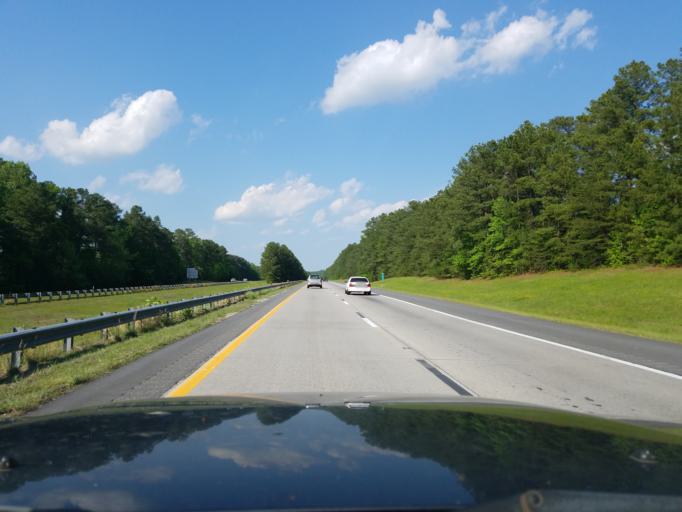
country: US
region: North Carolina
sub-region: Granville County
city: Creedmoor
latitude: 36.1731
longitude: -78.7043
